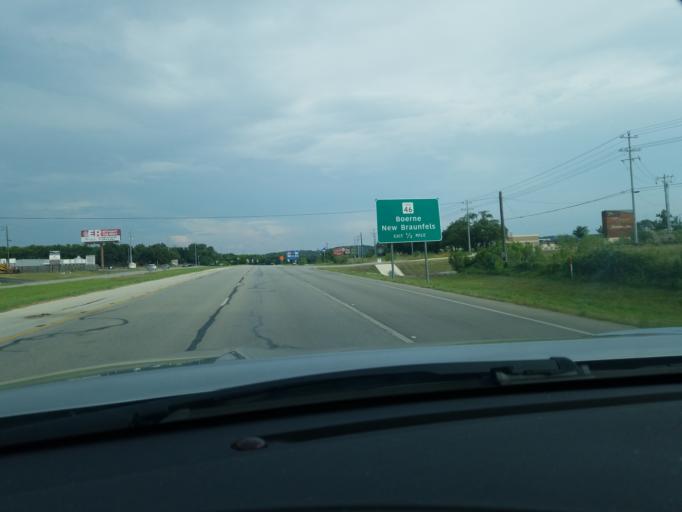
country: US
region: Texas
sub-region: Comal County
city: Bulverde
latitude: 29.8080
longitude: -98.4179
